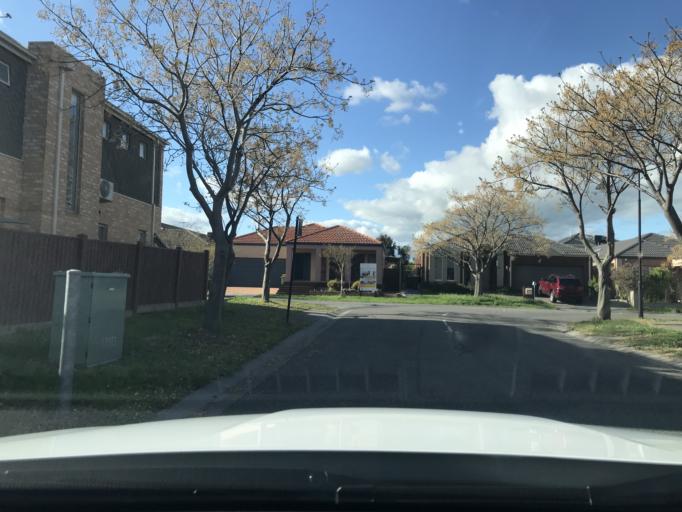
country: AU
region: Victoria
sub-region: Hume
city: Roxburgh Park
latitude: -37.5878
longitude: 144.9051
